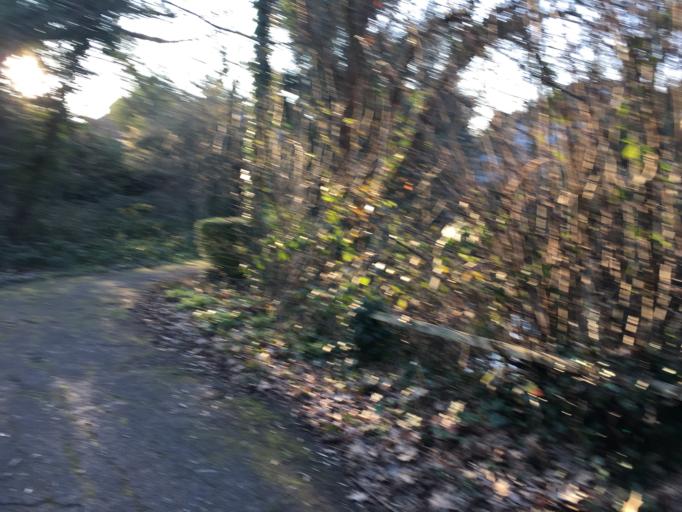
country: GB
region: England
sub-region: Greater London
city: Hendon
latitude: 51.5845
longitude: -0.2113
